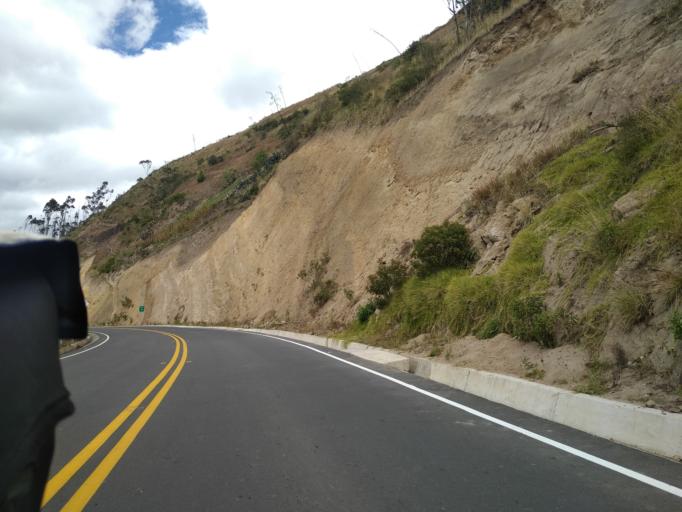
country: EC
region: Cotopaxi
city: Saquisili
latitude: -0.7081
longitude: -78.8824
